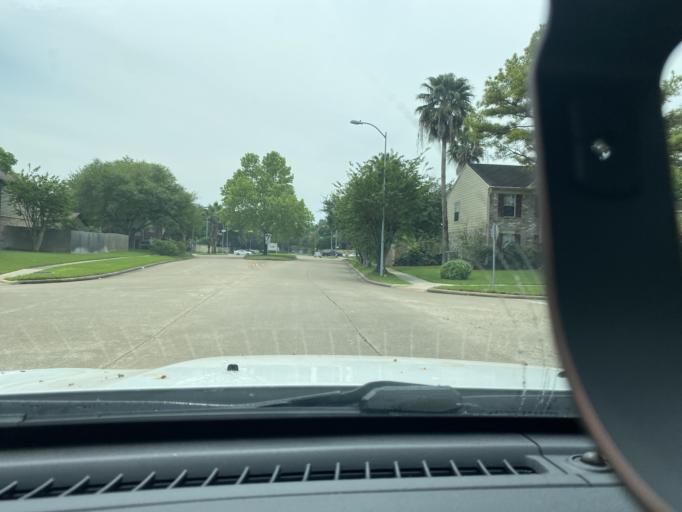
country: US
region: Texas
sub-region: Harris County
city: Jersey Village
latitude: 29.9103
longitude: -95.5735
